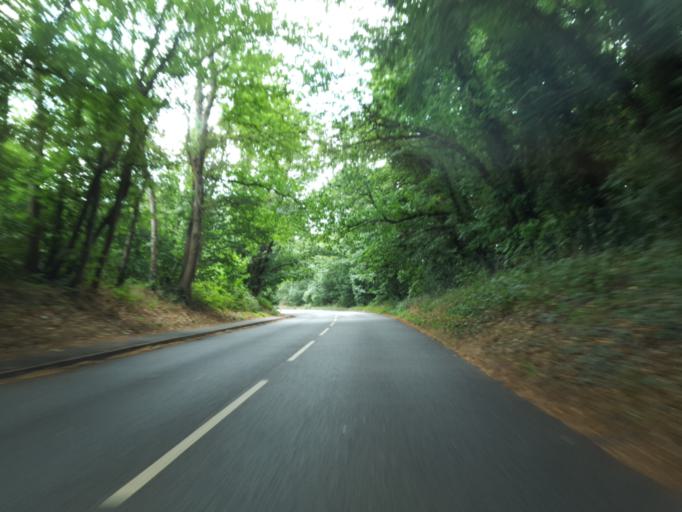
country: GB
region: England
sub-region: Kent
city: Boxley
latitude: 51.2910
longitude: 0.5248
